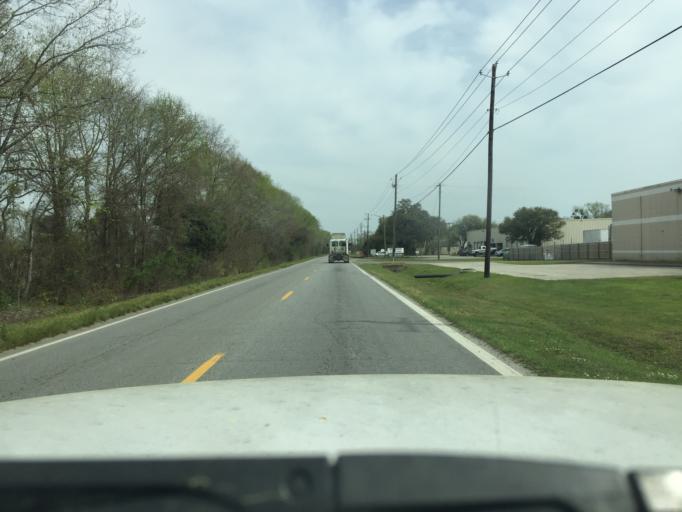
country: US
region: Georgia
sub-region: Chatham County
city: Savannah
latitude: 32.0830
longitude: -81.1268
